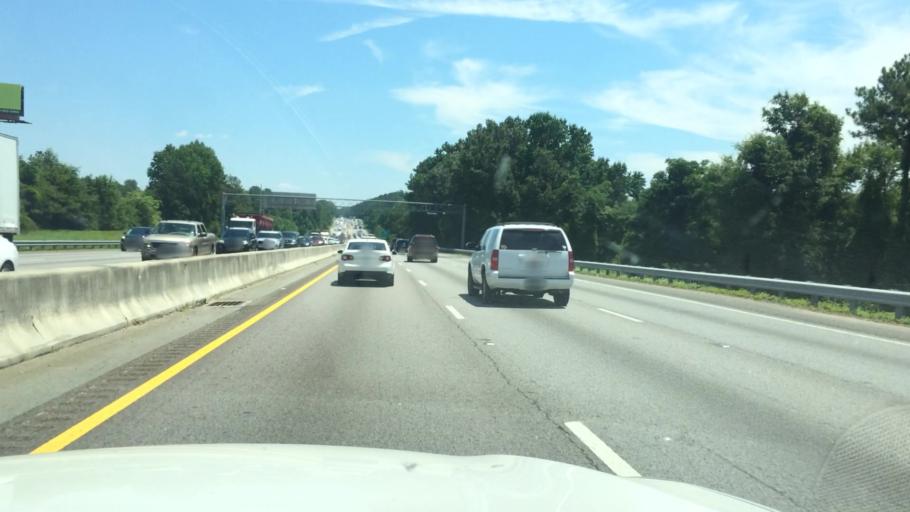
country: US
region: South Carolina
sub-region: Lexington County
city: West Columbia
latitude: 34.0505
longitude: -81.0671
